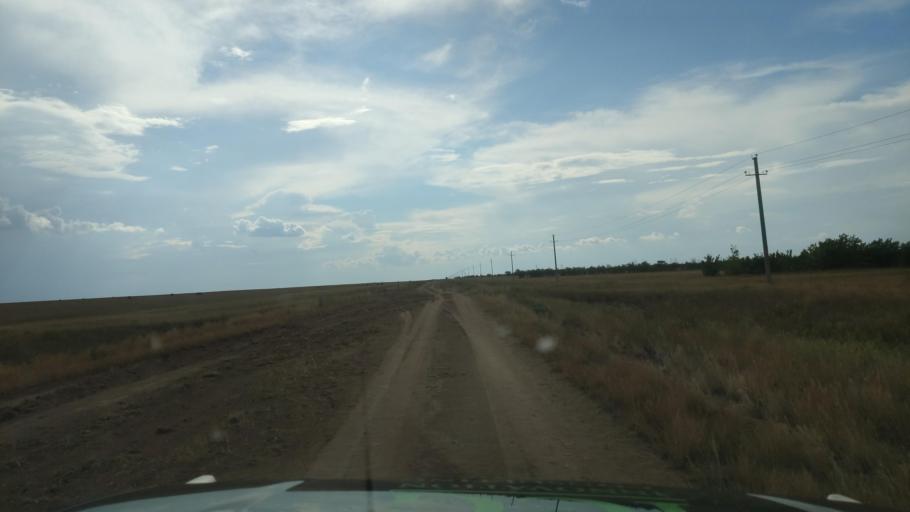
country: KZ
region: Pavlodar
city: Pavlodar
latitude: 52.5125
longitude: 77.5097
